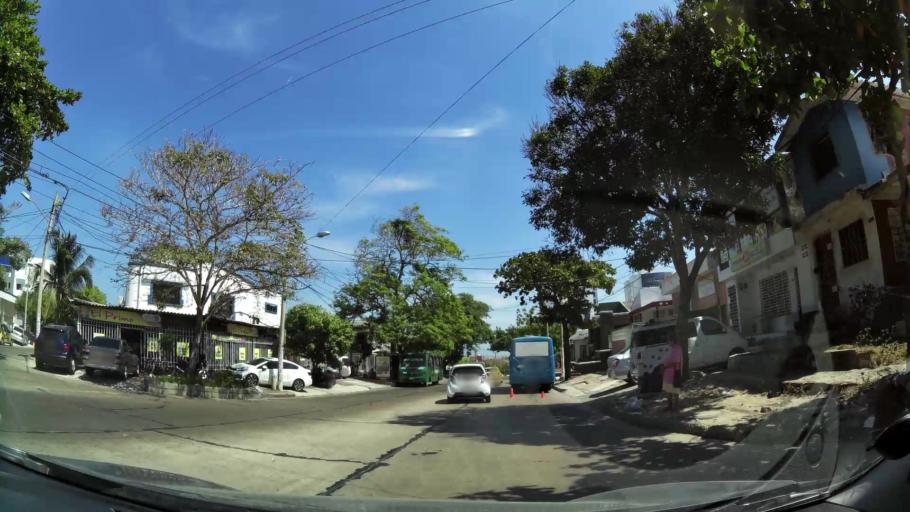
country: CO
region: Atlantico
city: Barranquilla
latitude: 10.9840
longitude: -74.8062
